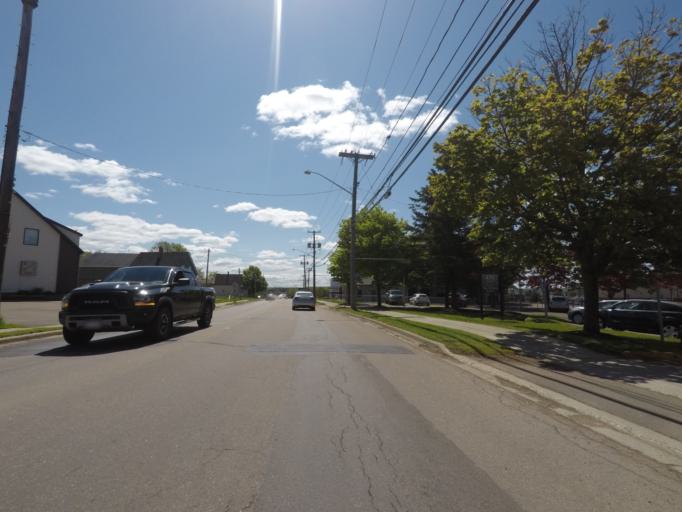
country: CA
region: New Brunswick
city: Moncton
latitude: 46.0963
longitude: -64.7529
